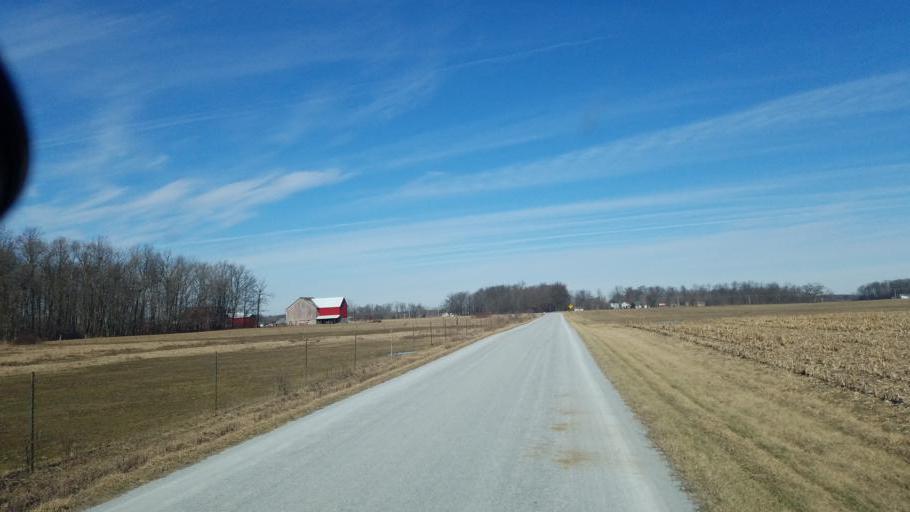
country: US
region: Ohio
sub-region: Hardin County
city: Kenton
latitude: 40.5811
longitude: -83.4709
